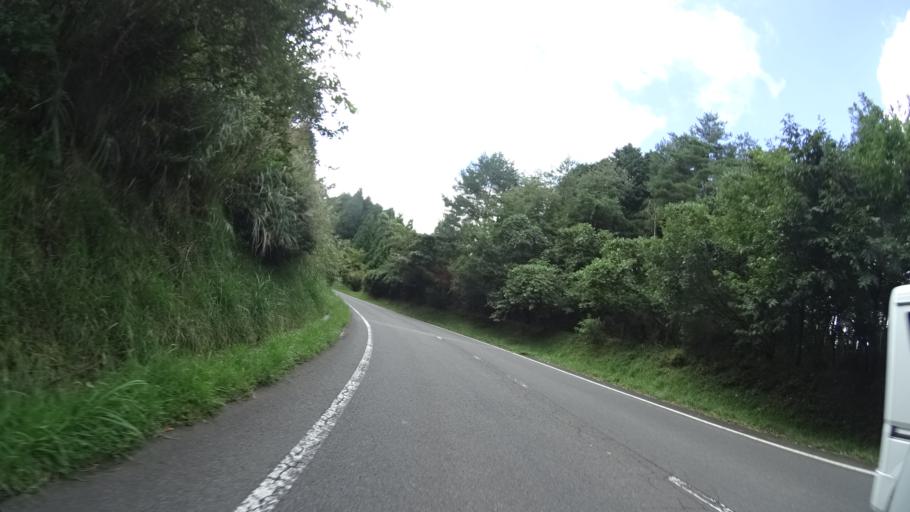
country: JP
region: Oita
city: Beppu
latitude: 33.3265
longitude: 131.4174
